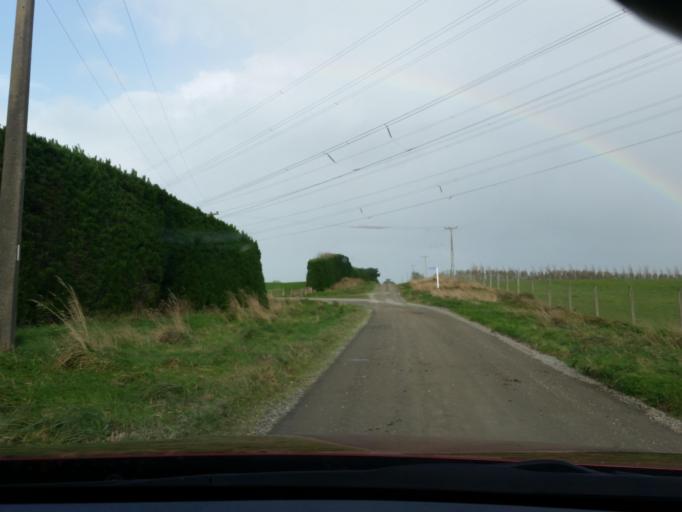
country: NZ
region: Southland
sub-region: Invercargill City
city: Invercargill
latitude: -46.3090
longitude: 168.3662
